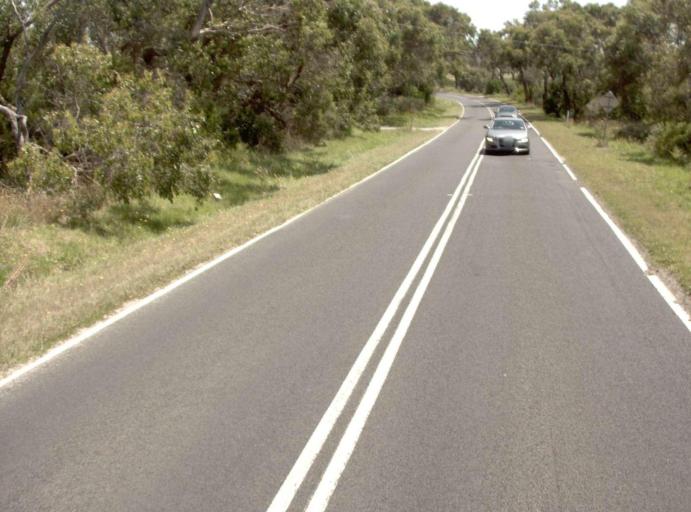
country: AU
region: Victoria
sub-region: Bass Coast
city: North Wonthaggi
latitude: -38.6464
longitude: 145.8526
